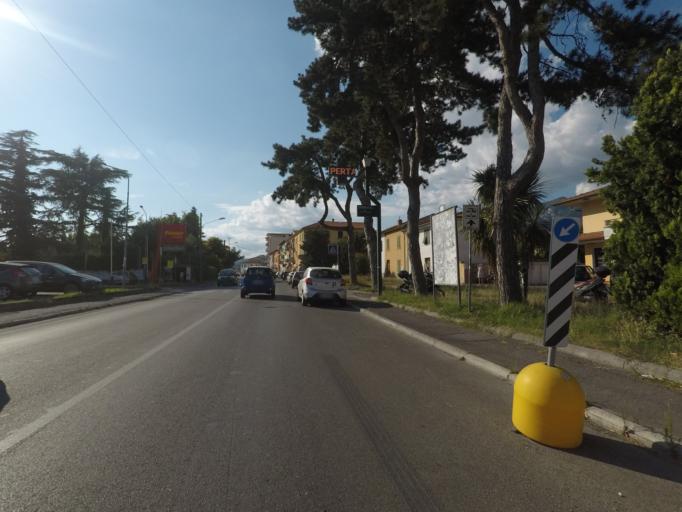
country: IT
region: Tuscany
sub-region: Provincia di Massa-Carrara
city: Massa
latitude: 44.0235
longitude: 10.1383
